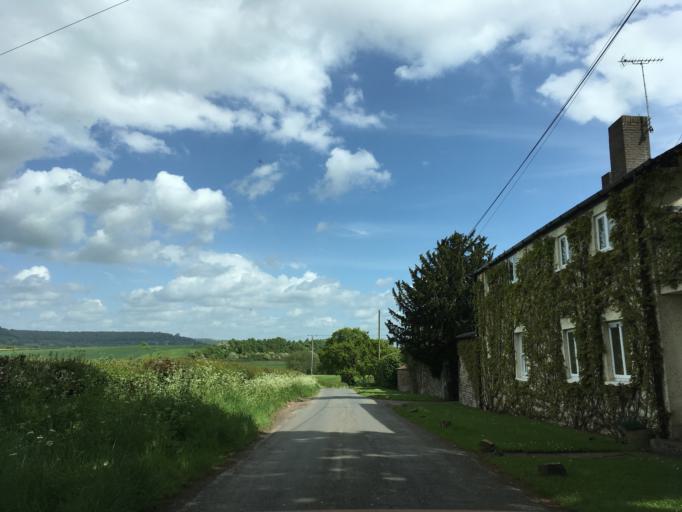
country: GB
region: England
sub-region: South Gloucestershire
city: Charfield
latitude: 51.6470
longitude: -2.4211
